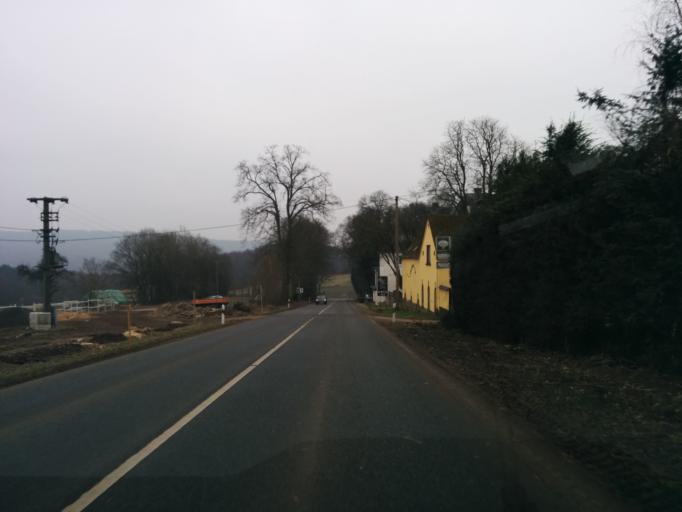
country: DE
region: Rheinland-Pfalz
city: Eitelborn
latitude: 50.3614
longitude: 7.7039
